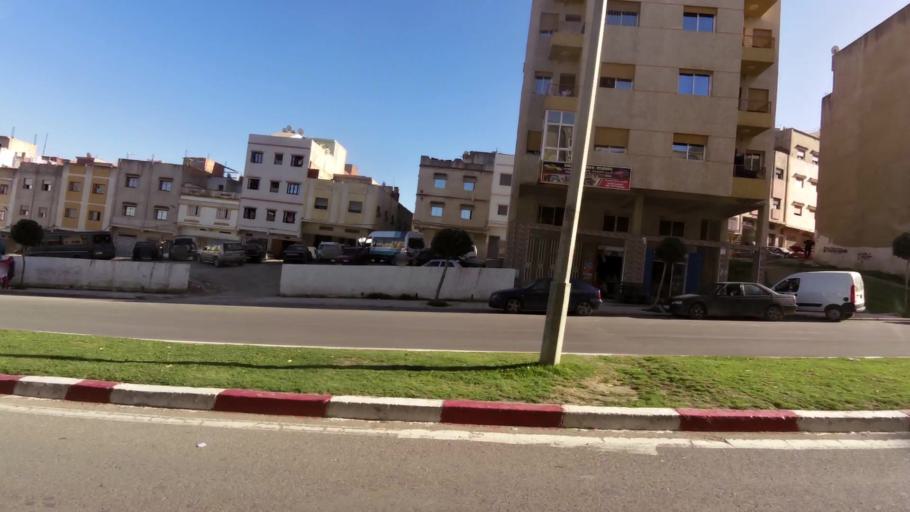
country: MA
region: Tanger-Tetouan
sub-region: Tanger-Assilah
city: Tangier
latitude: 35.7419
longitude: -5.8031
